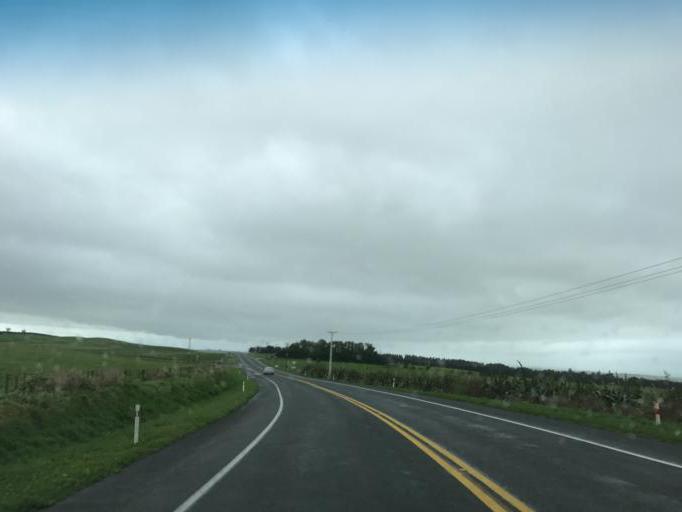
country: NZ
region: Manawatu-Wanganui
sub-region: Wanganui District
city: Wanganui
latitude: -39.8135
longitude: 174.7941
